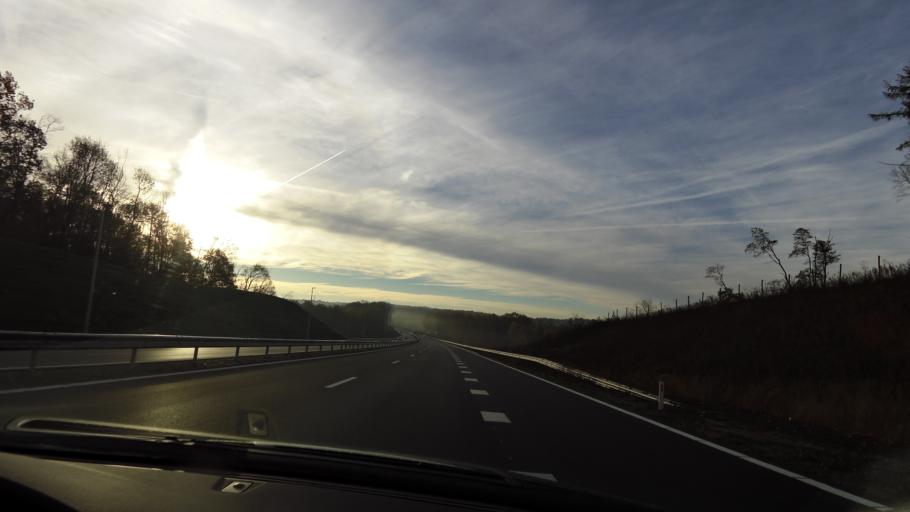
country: NL
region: Limburg
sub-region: Gemeente Brunssum
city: Brunssum
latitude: 50.9392
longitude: 5.9986
